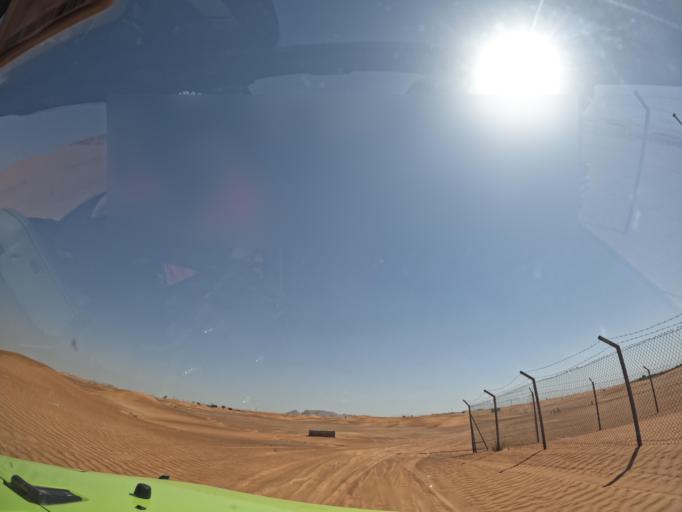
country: AE
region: Ash Shariqah
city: Adh Dhayd
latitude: 25.0114
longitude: 55.7380
